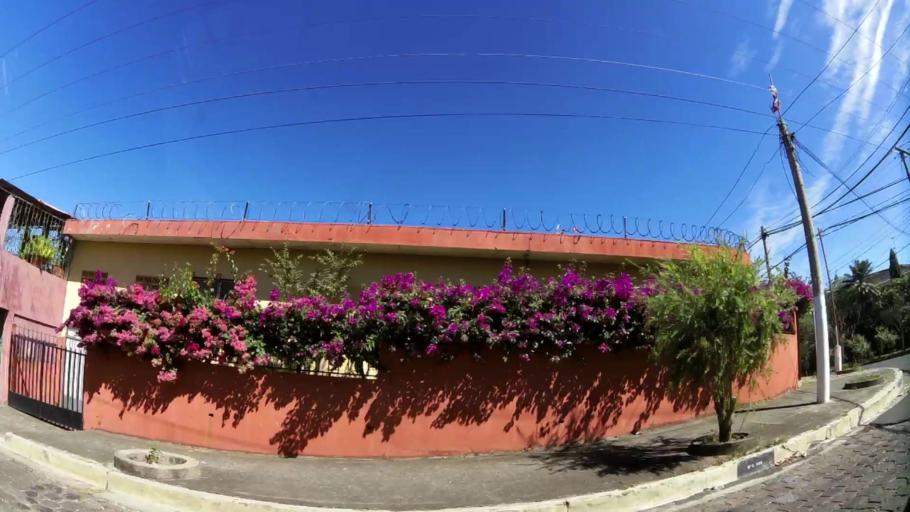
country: SV
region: Ahuachapan
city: Ahuachapan
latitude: 13.9176
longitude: -89.8520
